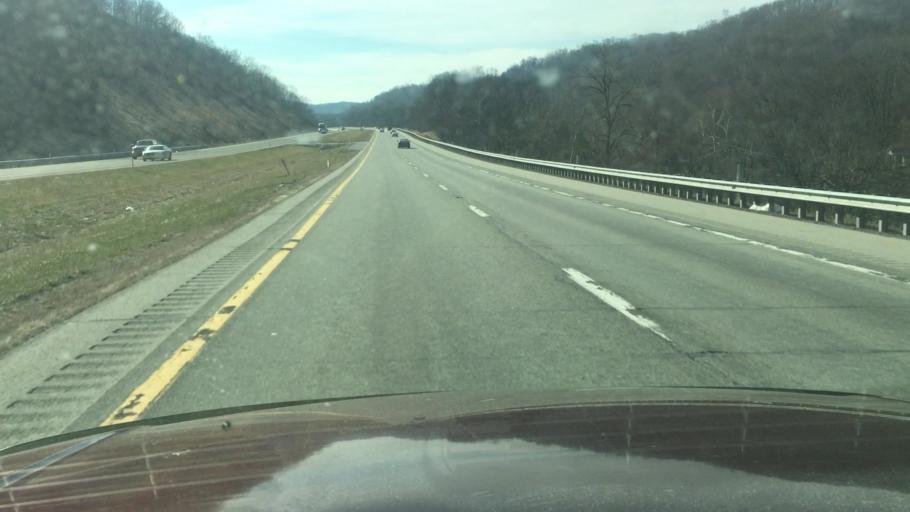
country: US
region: West Virginia
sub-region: Monongalia County
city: Star City
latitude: 39.7565
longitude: -80.0806
